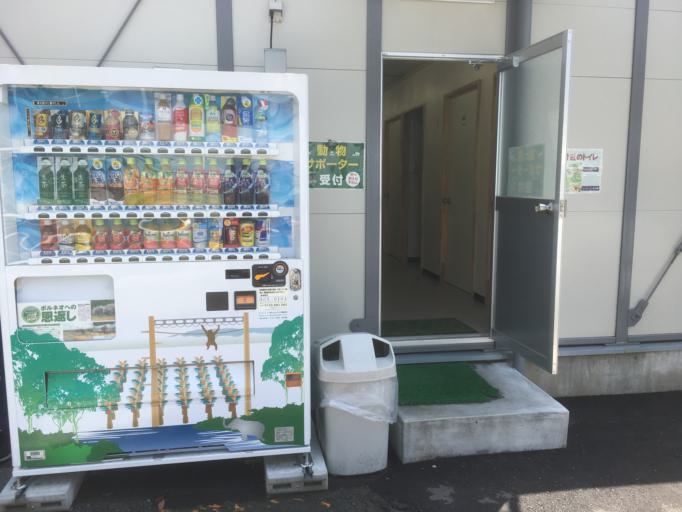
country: JP
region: Fukuoka
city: Fukuoka-shi
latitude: 33.5729
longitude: 130.3914
